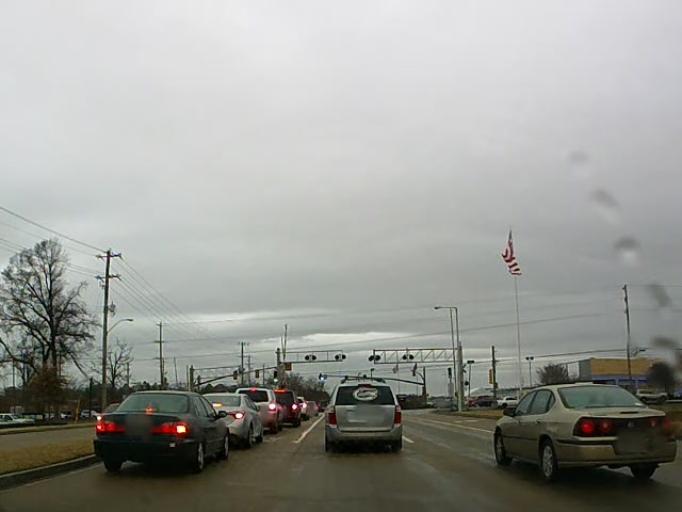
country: US
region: Tennessee
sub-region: Shelby County
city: Collierville
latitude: 35.0509
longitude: -89.7325
